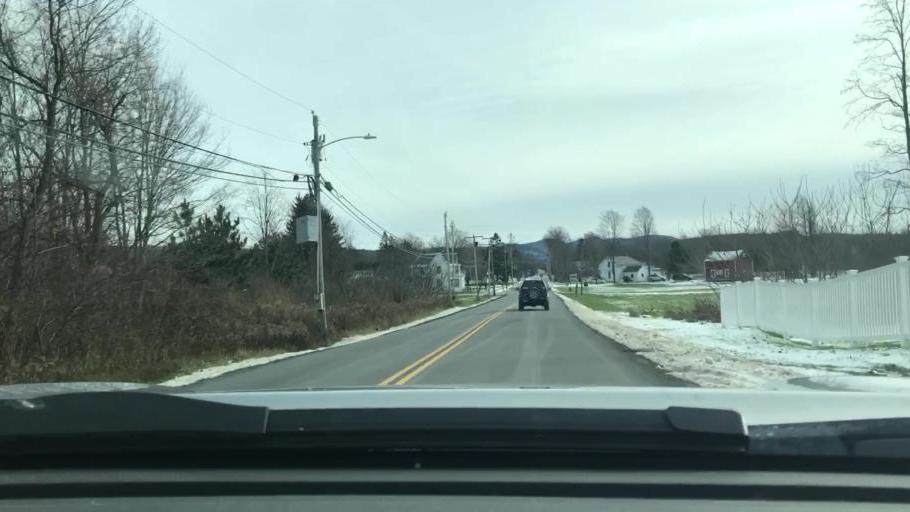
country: US
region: Vermont
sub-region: Rutland County
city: Poultney
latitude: 43.5255
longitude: -73.2457
